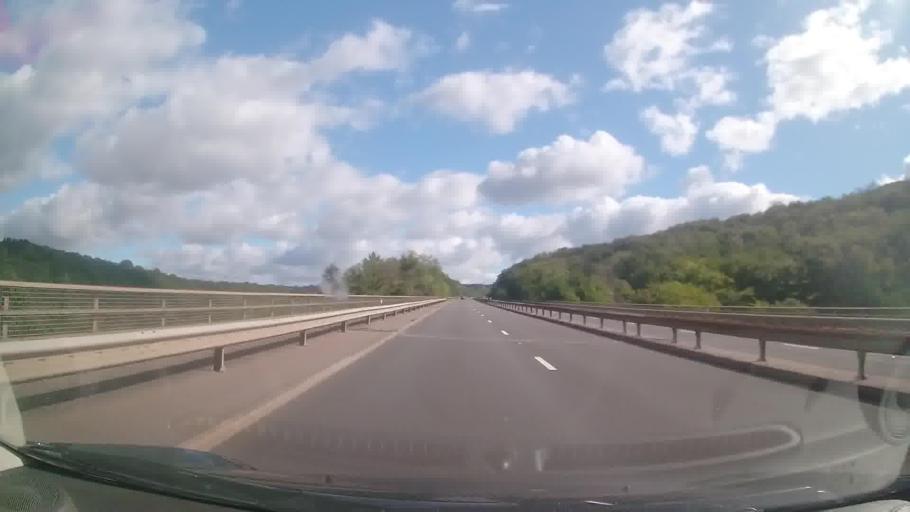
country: GB
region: Wales
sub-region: Neath Port Talbot
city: Glyn-neath
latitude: 51.7551
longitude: -3.5906
